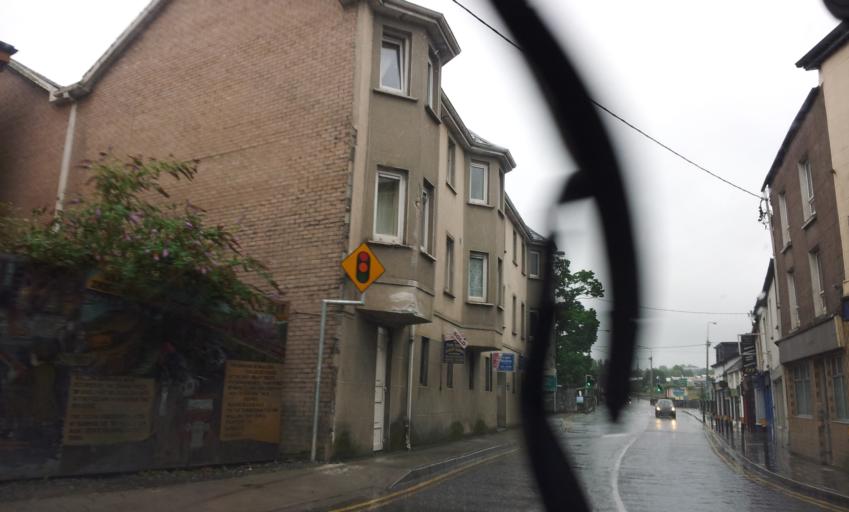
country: IE
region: Munster
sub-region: County Cork
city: Mallow
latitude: 52.1346
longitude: -8.6408
